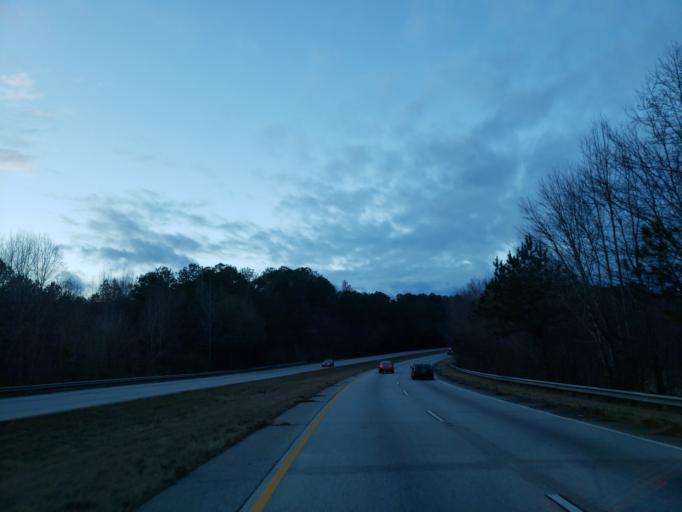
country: US
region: Georgia
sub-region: Fulton County
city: Union City
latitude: 33.6859
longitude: -84.5703
